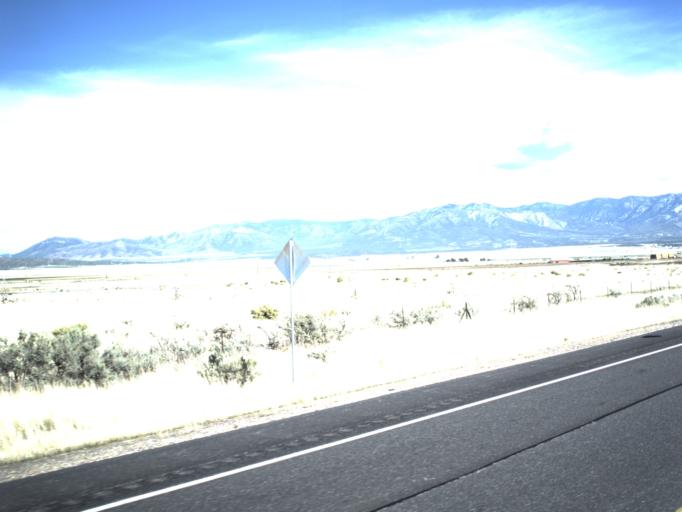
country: US
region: Utah
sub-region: Millard County
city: Fillmore
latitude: 39.1358
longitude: -112.3648
